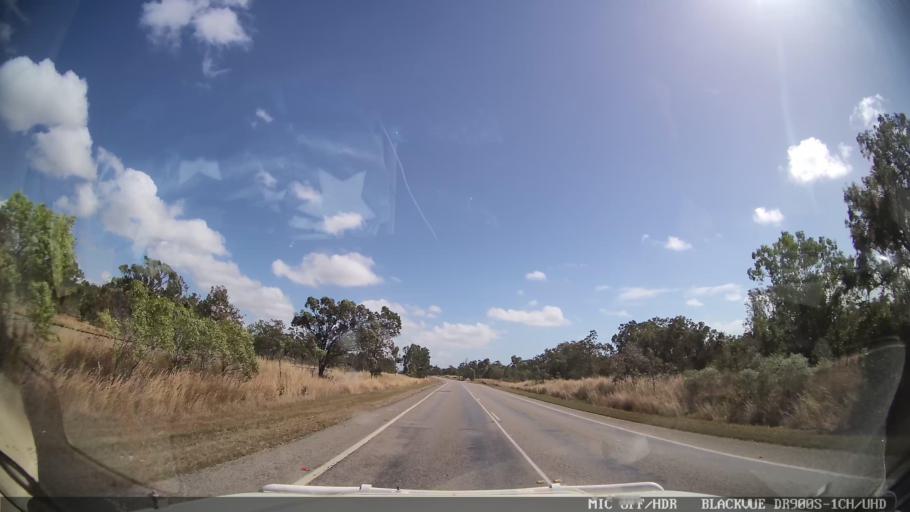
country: AU
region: Queensland
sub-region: Whitsunday
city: Bowen
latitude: -20.1790
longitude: 148.3489
